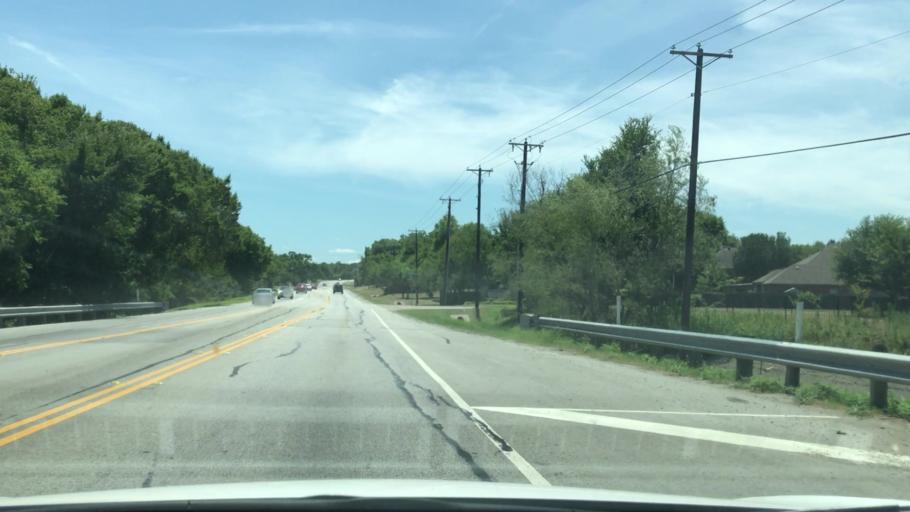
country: US
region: Texas
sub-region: Rockwall County
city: Rockwall
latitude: 32.9476
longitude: -96.4618
